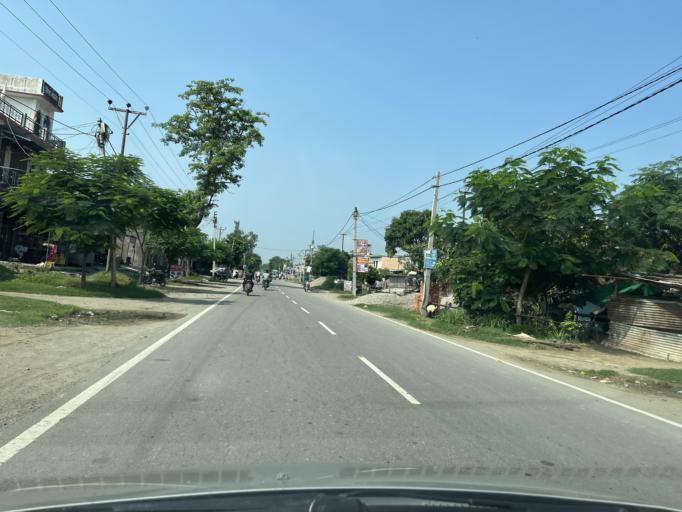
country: IN
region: Uttarakhand
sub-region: Udham Singh Nagar
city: Bazpur
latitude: 29.2061
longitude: 79.2105
